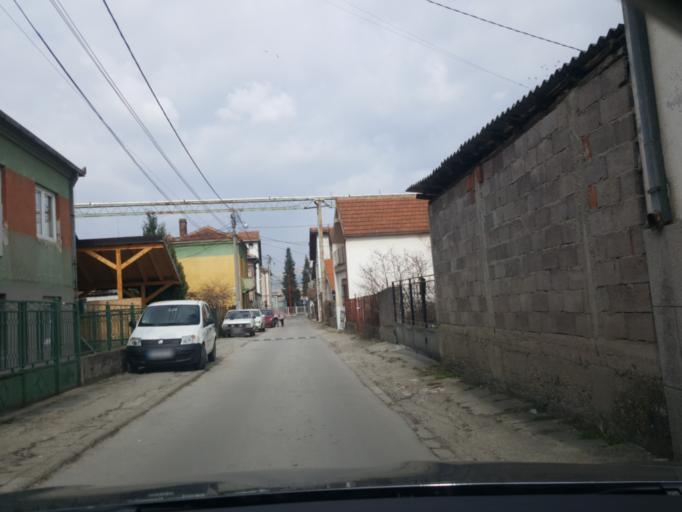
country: RS
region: Central Serbia
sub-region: Nisavski Okrug
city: Nis
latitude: 43.3143
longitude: 21.8717
